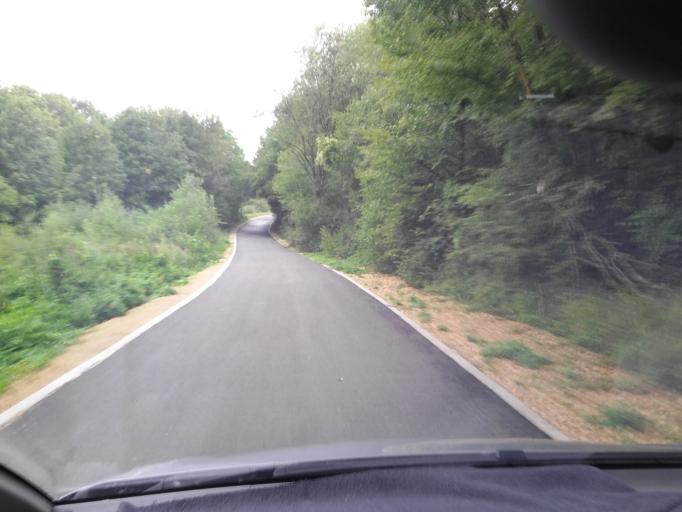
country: BE
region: Wallonia
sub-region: Province du Luxembourg
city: Attert
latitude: 49.7344
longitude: 5.8052
